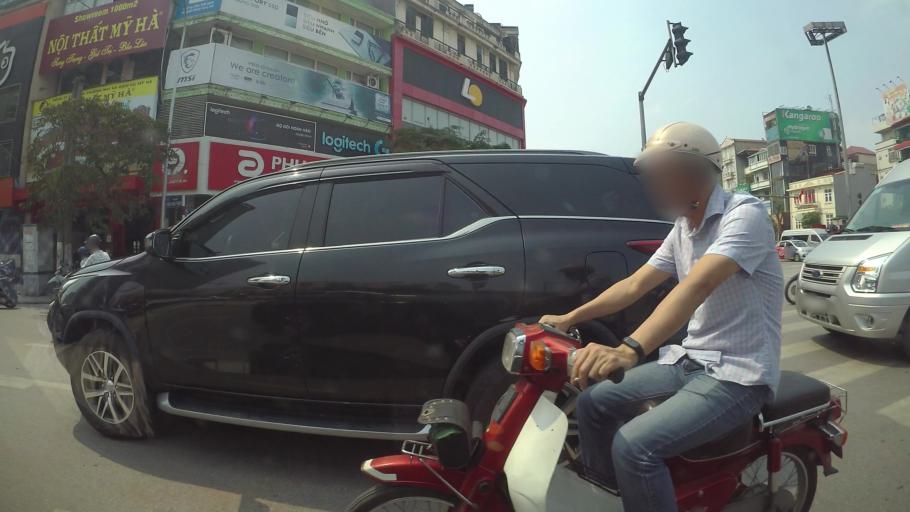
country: VN
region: Ha Noi
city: Dong Da
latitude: 21.0110
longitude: 105.8369
